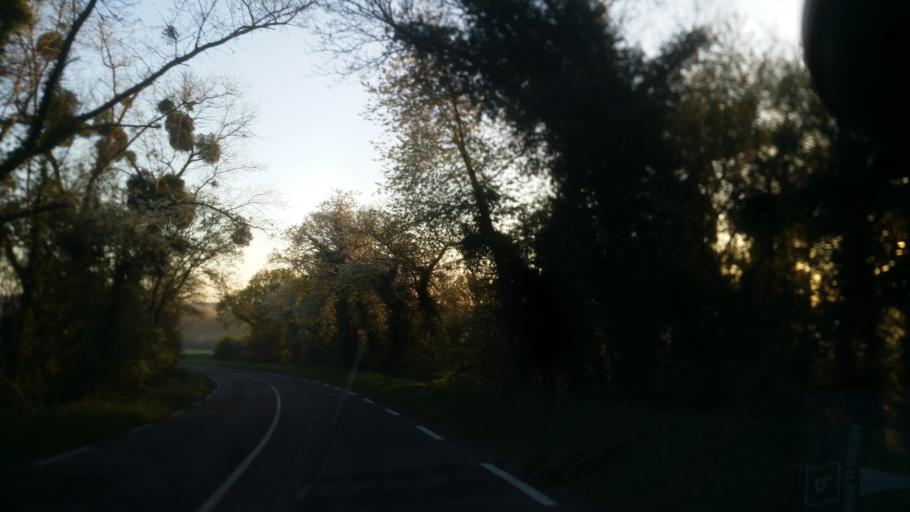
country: FR
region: Ile-de-France
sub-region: Departement de l'Essonne
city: Saint-Cyr-sous-Dourdan
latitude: 48.5524
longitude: 2.0249
